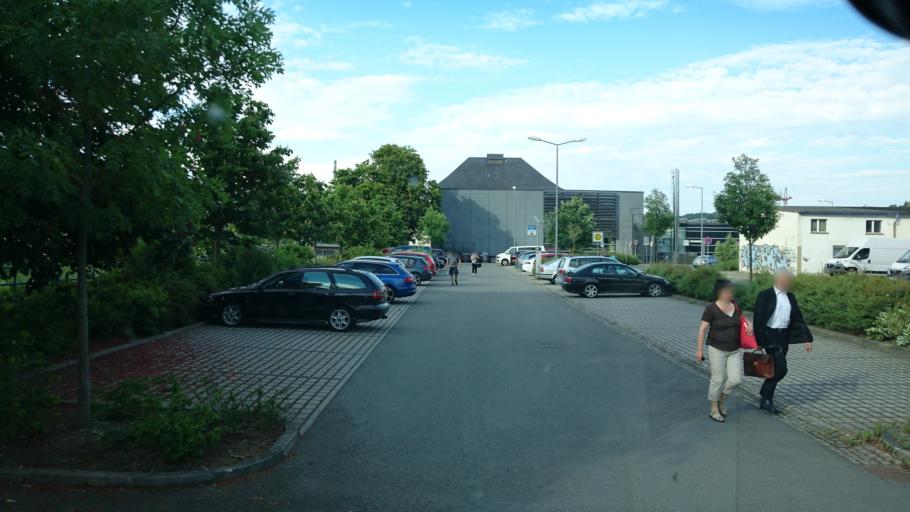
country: DE
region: Saxony
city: Plauen
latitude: 50.4907
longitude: 12.1385
